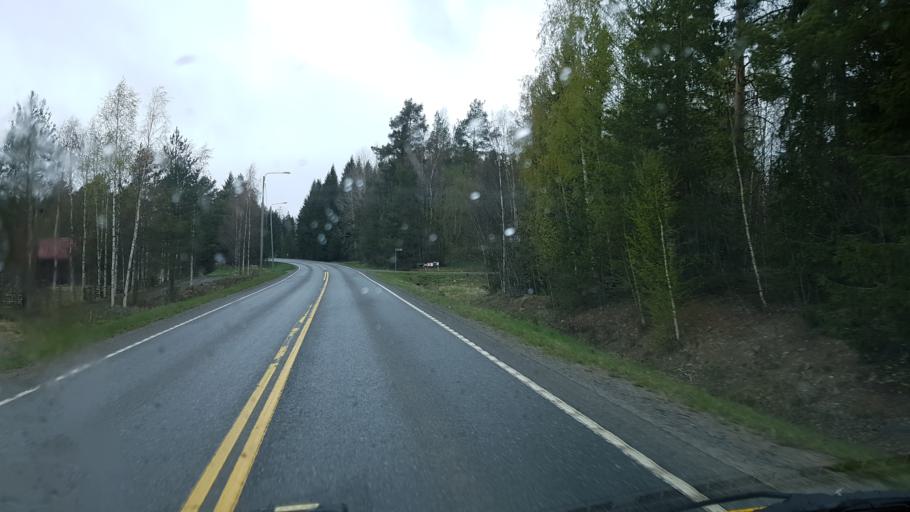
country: FI
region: Pirkanmaa
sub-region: Tampere
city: Pirkkala
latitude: 61.4268
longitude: 23.6328
